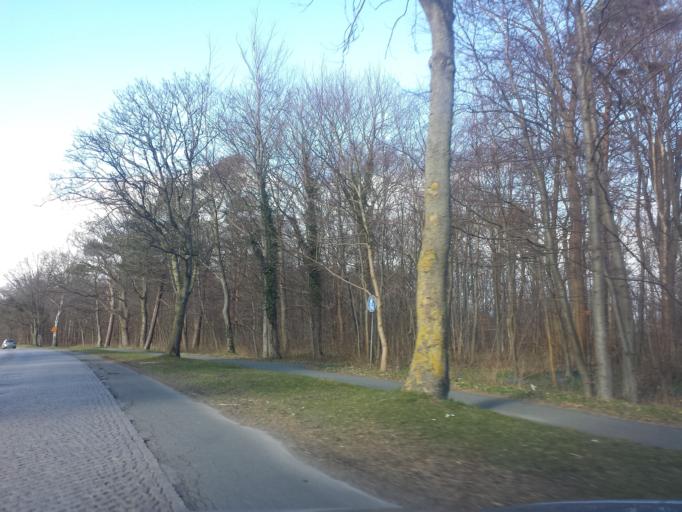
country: SE
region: Skane
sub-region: Simrishamns Kommun
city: Simrishamn
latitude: 55.5657
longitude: 14.3358
